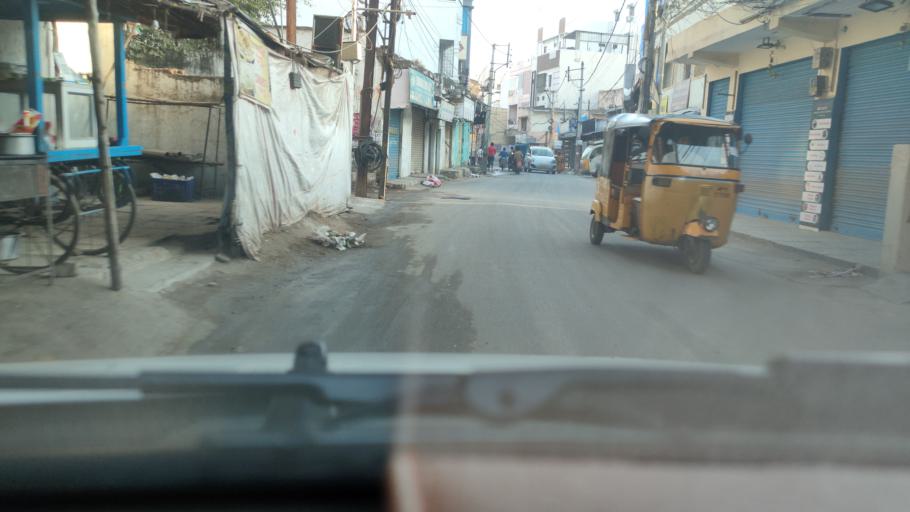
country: IN
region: Telangana
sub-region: Hyderabad
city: Malkajgiri
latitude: 17.4109
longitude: 78.5080
